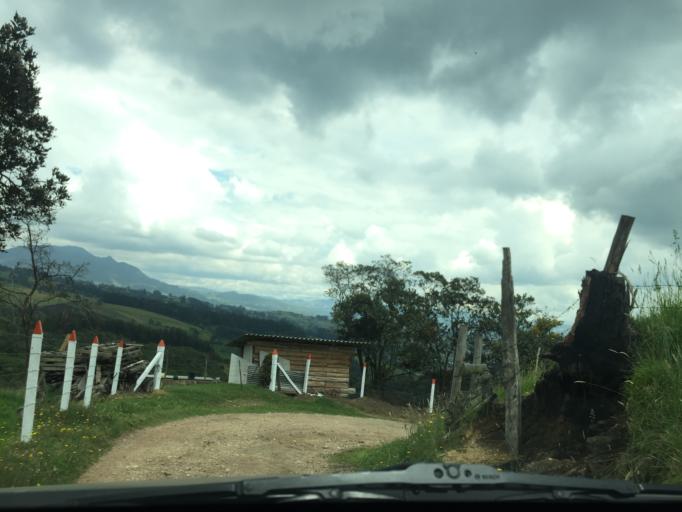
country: CO
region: Cundinamarca
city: Cogua
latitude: 5.0548
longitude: -74.0109
